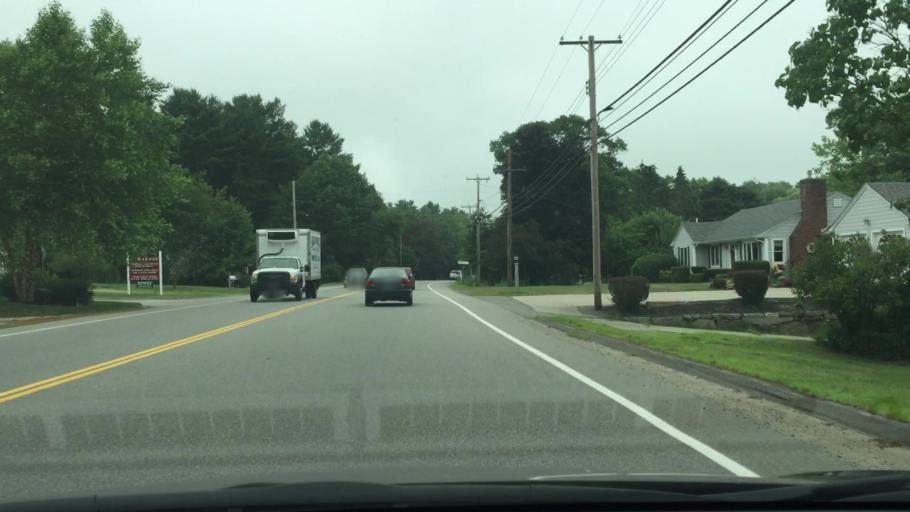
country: US
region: Maine
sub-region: York County
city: Cape Neddick
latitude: 43.1838
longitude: -70.6244
